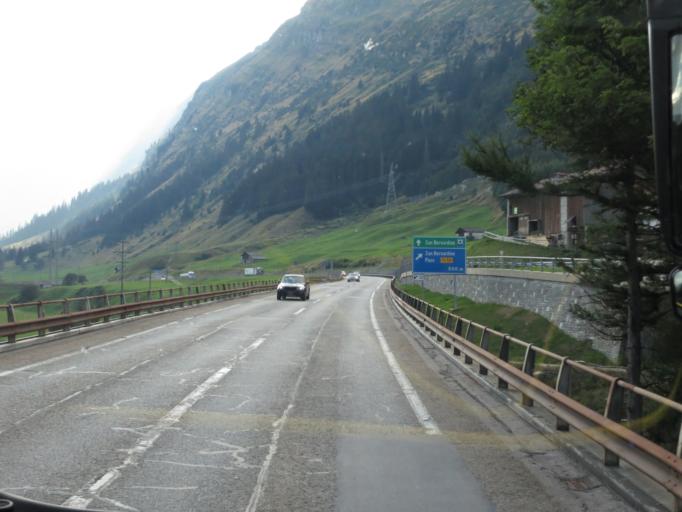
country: CH
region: Grisons
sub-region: Hinterrhein District
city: Hinterrhein
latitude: 46.5302
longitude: 9.1986
